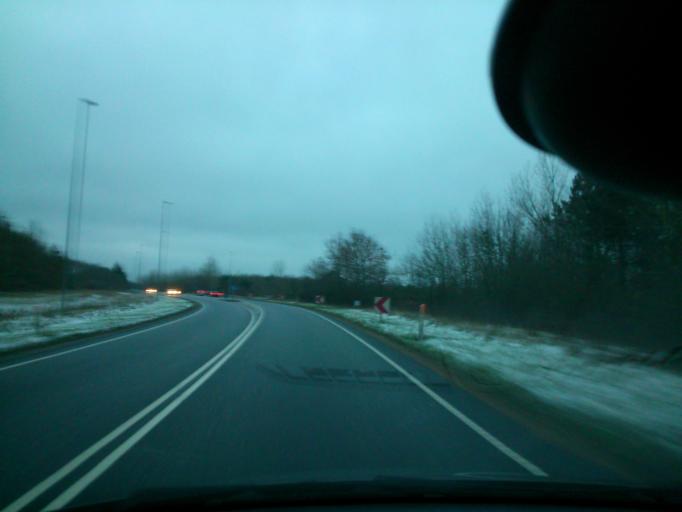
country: DK
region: Central Jutland
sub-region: Ringkobing-Skjern Kommune
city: Tarm
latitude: 55.9045
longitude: 8.5041
